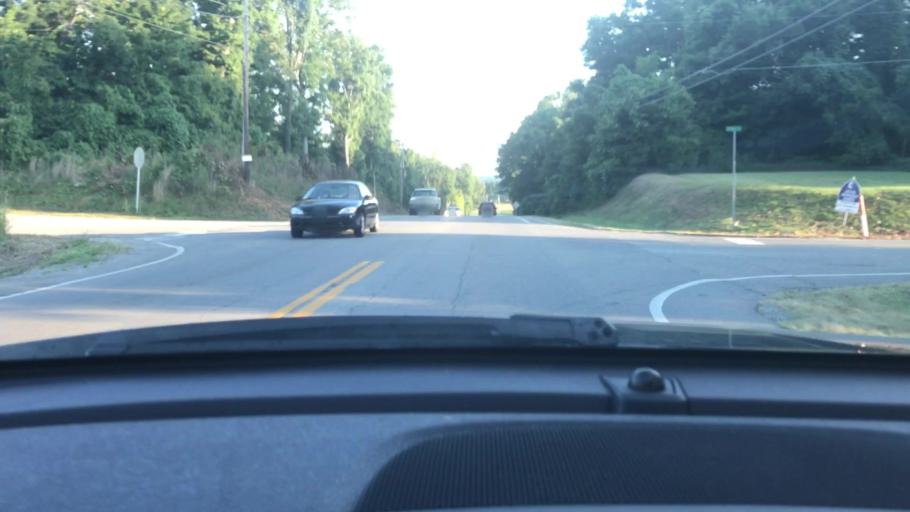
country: US
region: Tennessee
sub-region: Dickson County
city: Charlotte
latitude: 36.1510
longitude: -87.3560
